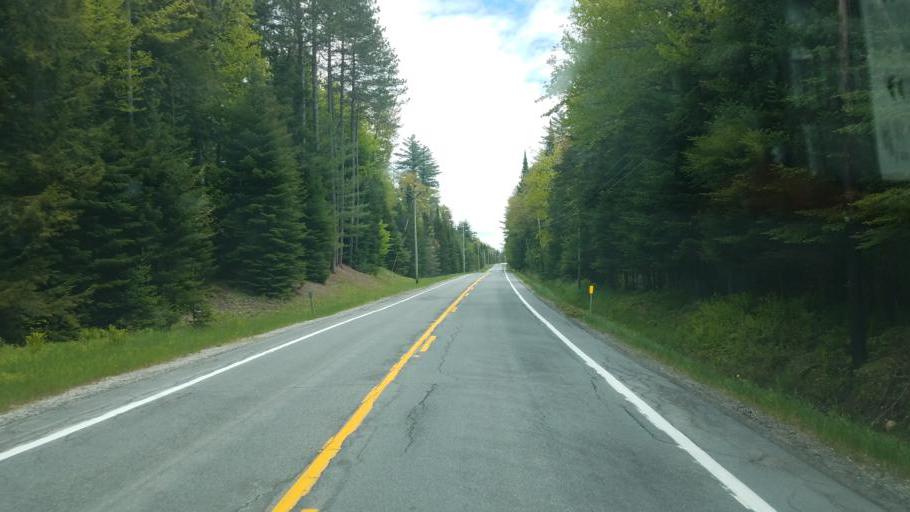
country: US
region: New York
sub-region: Hamilton County
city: Lake Pleasant
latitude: 43.8045
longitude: -74.6779
